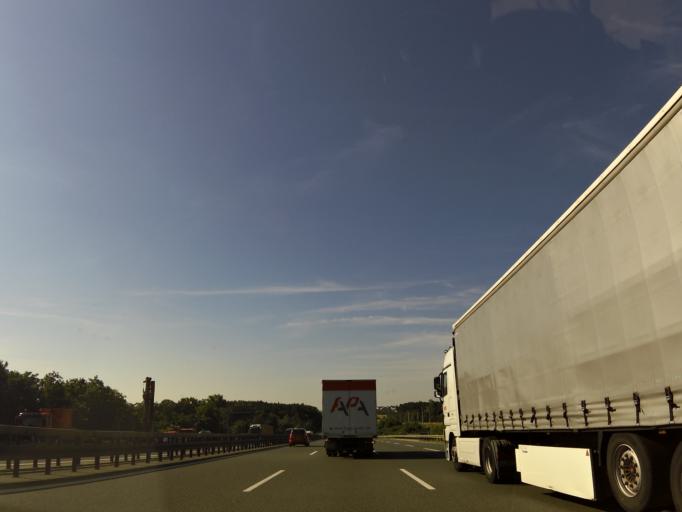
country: DE
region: Bavaria
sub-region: Regierungsbezirk Mittelfranken
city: Allersberg
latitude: 49.2494
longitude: 11.2163
